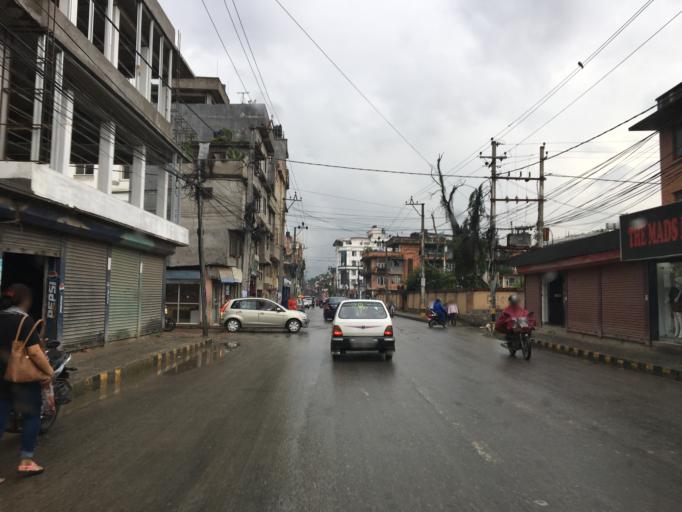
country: NP
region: Central Region
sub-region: Bagmati Zone
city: Kathmandu
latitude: 27.7119
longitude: 85.3321
